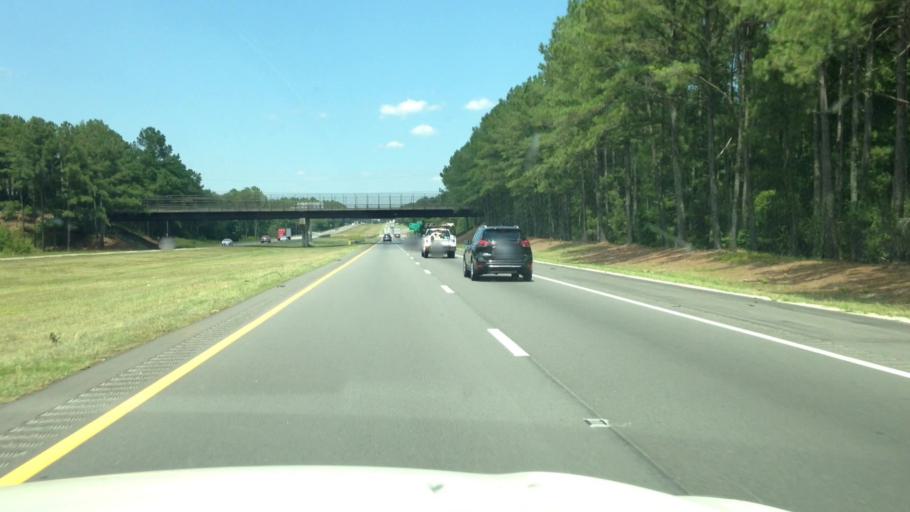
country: US
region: North Carolina
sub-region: Cumberland County
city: Hope Mills
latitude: 34.9553
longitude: -78.8968
